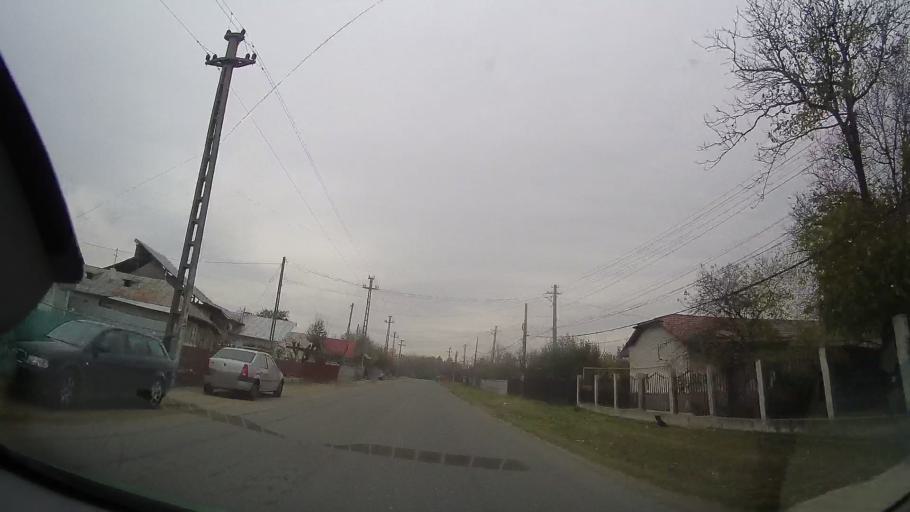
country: RO
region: Prahova
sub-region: Oras Urlati
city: Urlati
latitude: 45.0045
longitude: 26.2275
